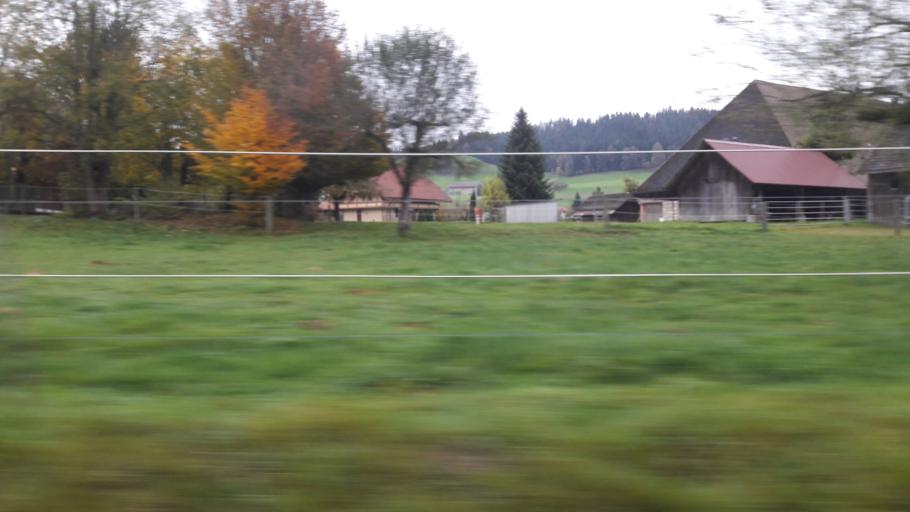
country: CH
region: Bern
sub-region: Emmental District
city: Trachselwald
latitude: 47.0158
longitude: 7.7268
